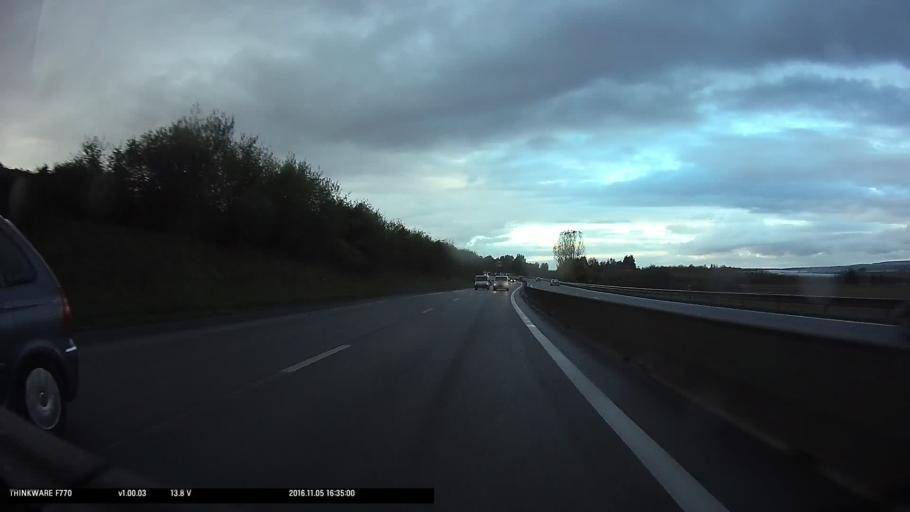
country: FR
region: Ile-de-France
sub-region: Departement du Val-d'Oise
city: Ableiges
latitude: 49.0676
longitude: 1.9722
